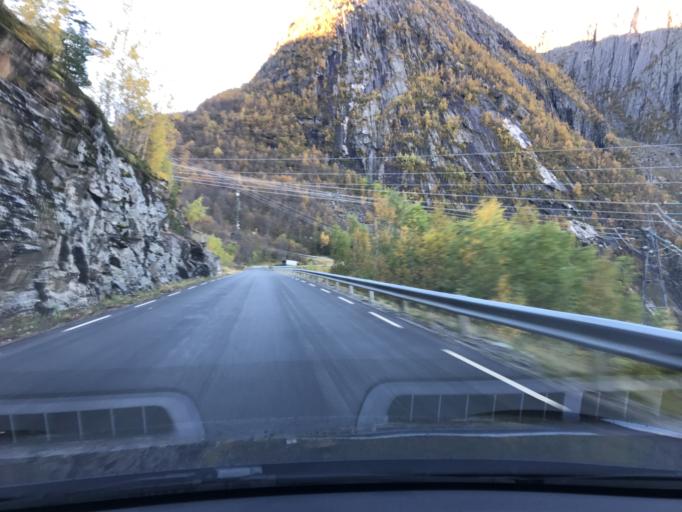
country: NO
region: Sogn og Fjordane
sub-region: Aurland
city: Aurlandsvangen
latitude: 60.8575
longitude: 7.3093
